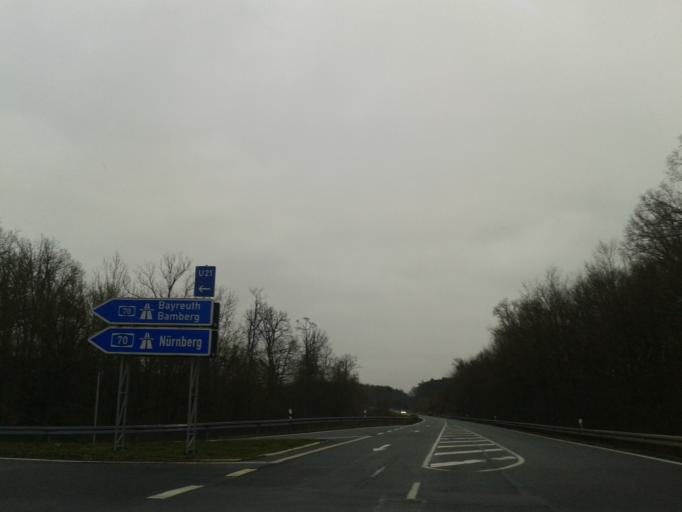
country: DE
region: Bavaria
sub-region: Regierungsbezirk Unterfranken
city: Wonfurt
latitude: 50.0020
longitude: 10.4360
